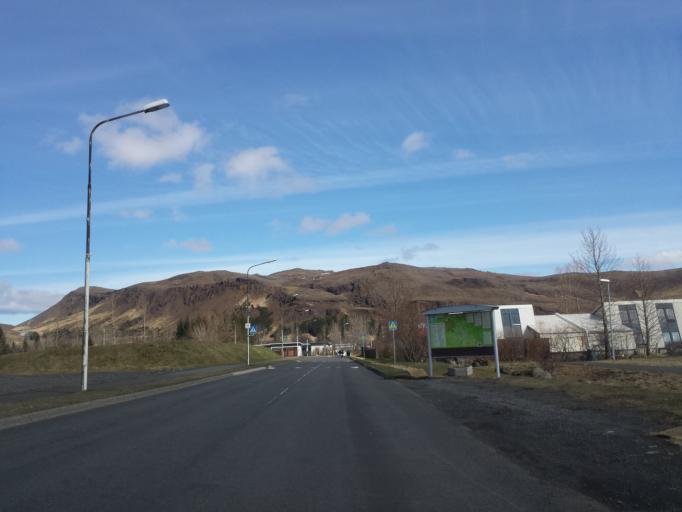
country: IS
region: South
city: Hveragerdi
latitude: 63.9938
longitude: -21.1837
